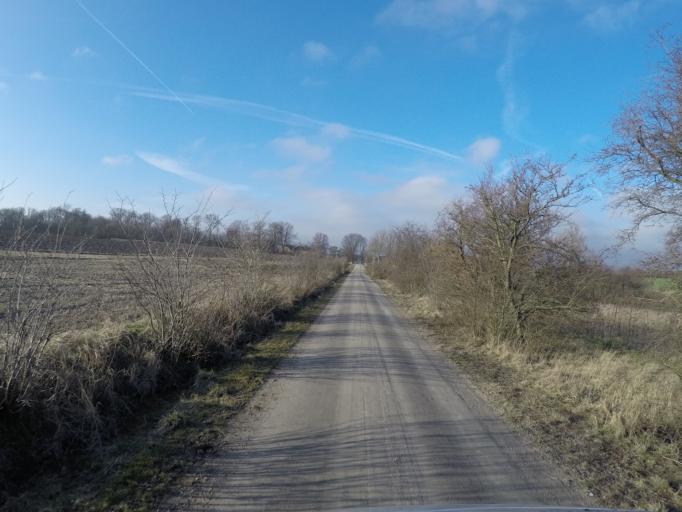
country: SE
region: Skane
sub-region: Lunds Kommun
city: Lund
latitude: 55.6936
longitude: 13.2714
